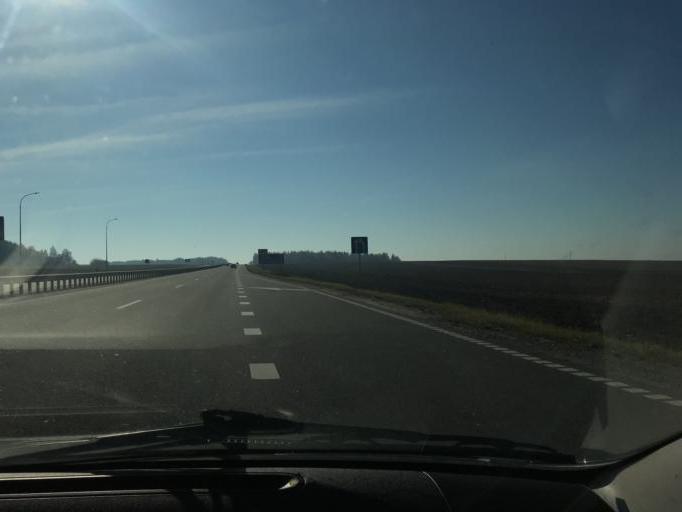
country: BY
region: Minsk
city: Slutsk
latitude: 53.2114
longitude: 27.5505
